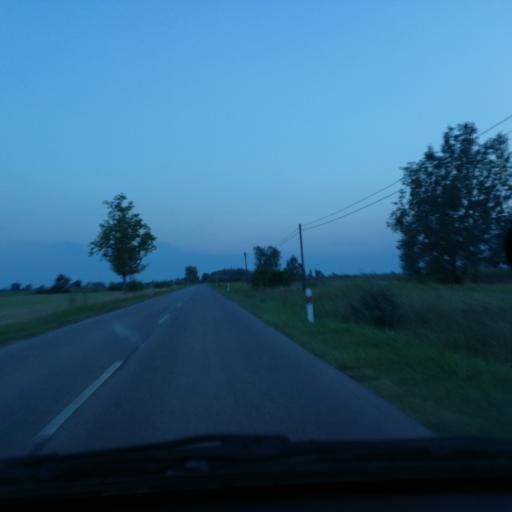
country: HU
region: Bacs-Kiskun
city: Kecel
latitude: 46.5324
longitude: 19.1294
